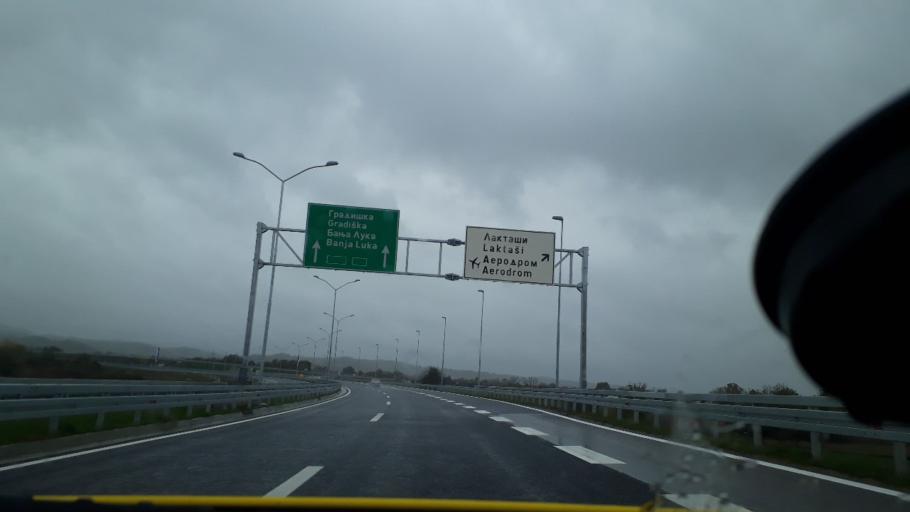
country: BA
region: Republika Srpska
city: Laktasi
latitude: 44.9179
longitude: 17.3323
